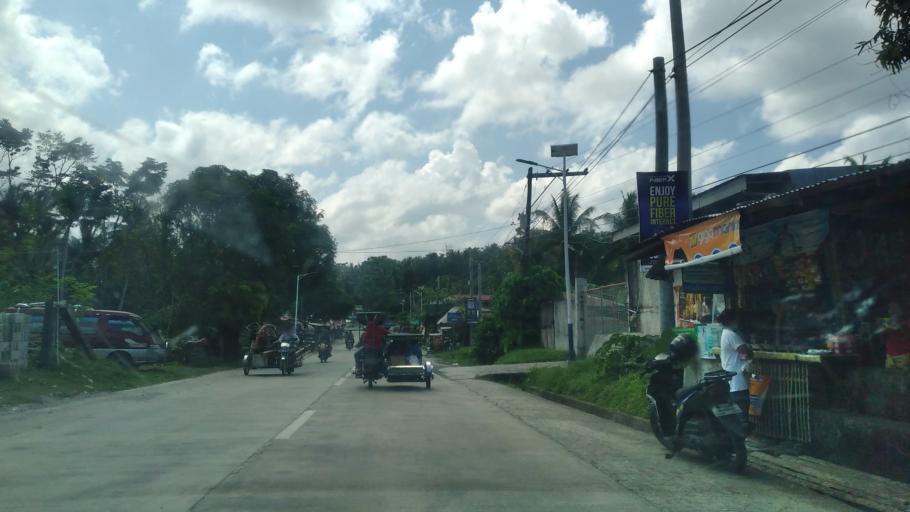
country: PH
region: Calabarzon
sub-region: Province of Quezon
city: Macalelon
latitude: 13.7569
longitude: 122.1435
